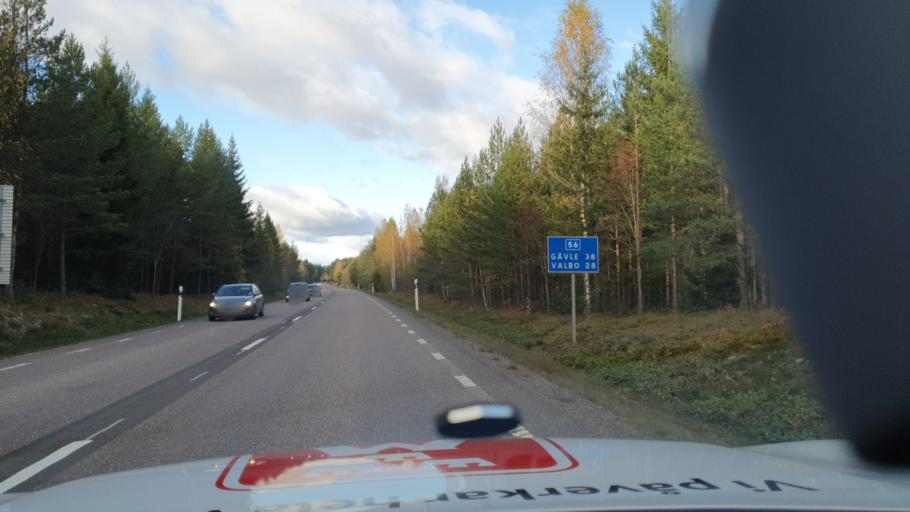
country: SE
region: Gaevleborg
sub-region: Gavle Kommun
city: Hedesunda
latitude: 60.3973
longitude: 16.9758
